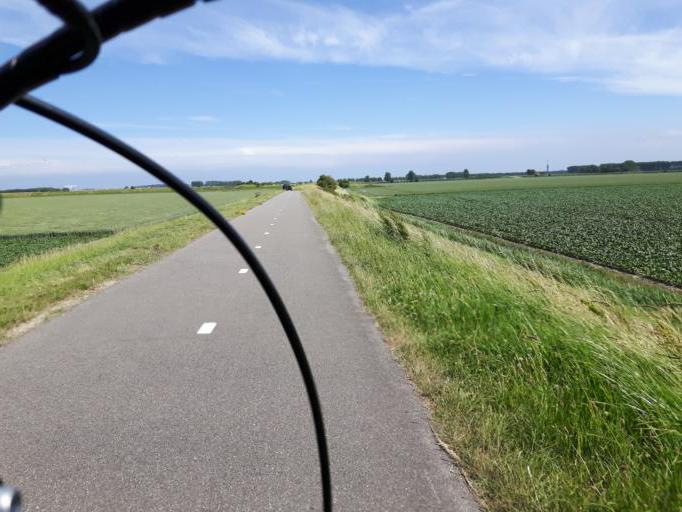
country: NL
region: Zeeland
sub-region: Gemeente Goes
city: Goes
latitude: 51.5438
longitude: 3.8316
